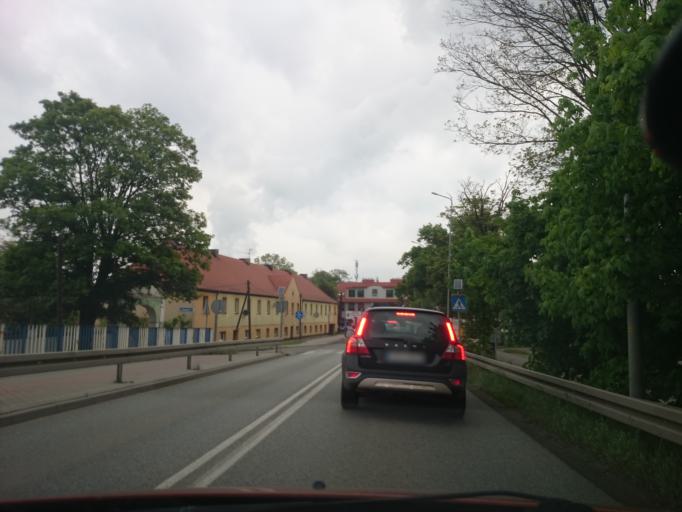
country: PL
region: Opole Voivodeship
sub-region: Powiat opolski
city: Czarnowasy
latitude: 50.7190
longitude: 17.9027
